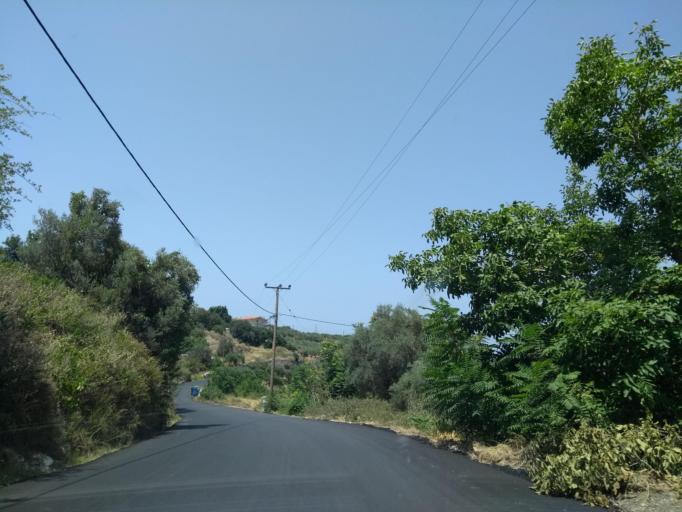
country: GR
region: Crete
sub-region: Nomos Chanias
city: Georgioupolis
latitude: 35.3183
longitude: 24.2992
